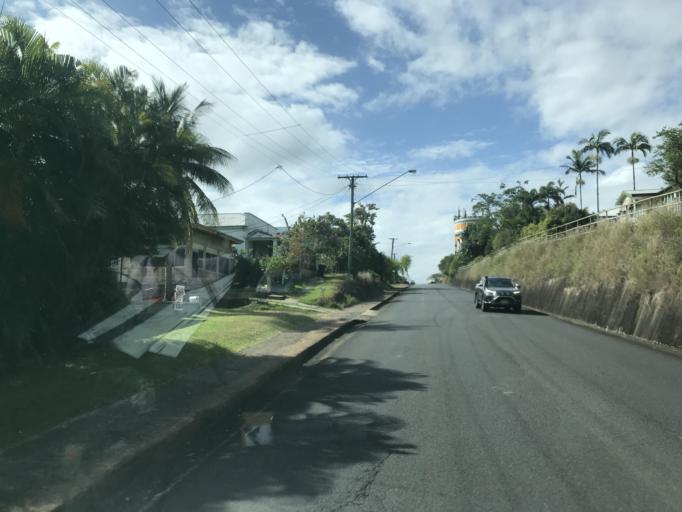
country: AU
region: Queensland
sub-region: Cassowary Coast
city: Innisfail
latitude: -17.5265
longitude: 146.0343
